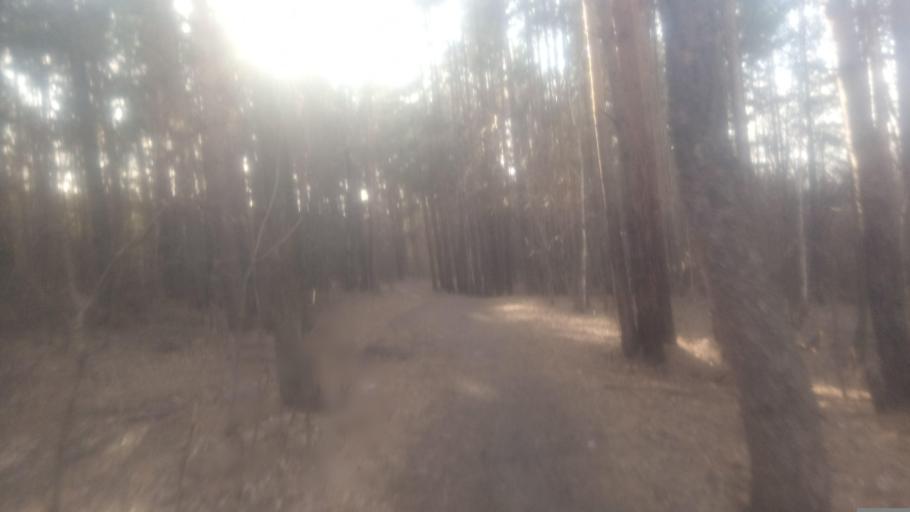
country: RU
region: Chelyabinsk
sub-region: Gorod Chelyabinsk
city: Chelyabinsk
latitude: 55.1664
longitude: 61.3402
